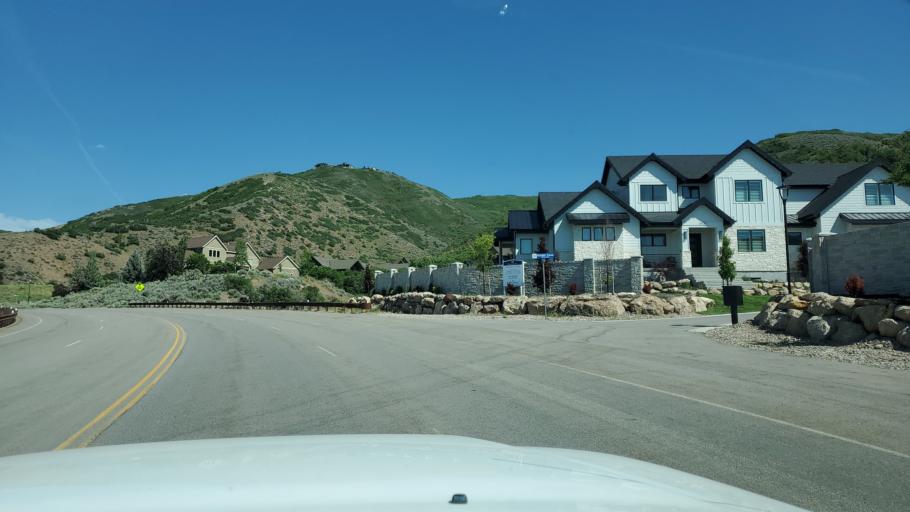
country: US
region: Utah
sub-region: Salt Lake County
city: Draper
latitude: 40.4844
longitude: -111.8671
